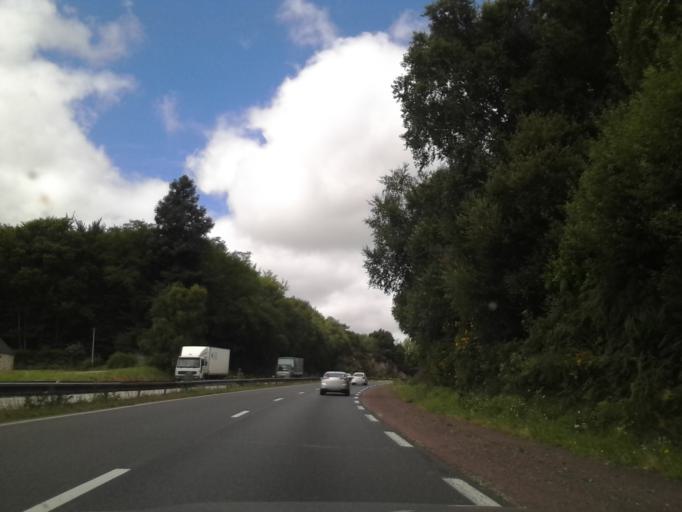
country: FR
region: Lower Normandy
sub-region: Departement de la Manche
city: Brix
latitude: 49.5474
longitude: -1.5594
